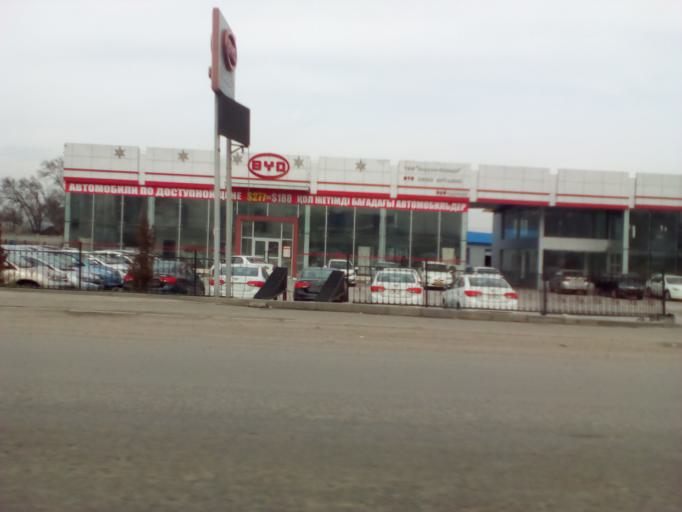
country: KZ
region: Almaty Oblysy
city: Burunday
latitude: 43.2288
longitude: 76.7606
